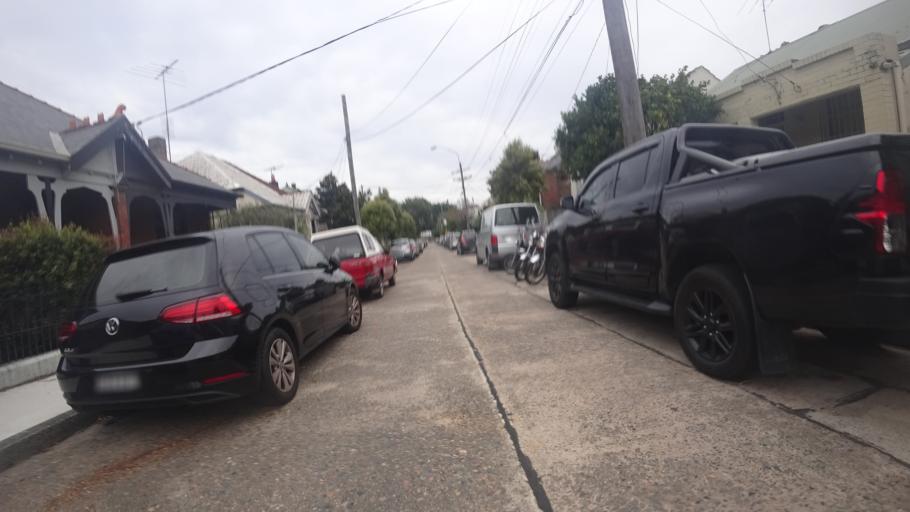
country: AU
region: New South Wales
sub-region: Marrickville
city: Newtown
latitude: -33.9079
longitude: 151.1770
